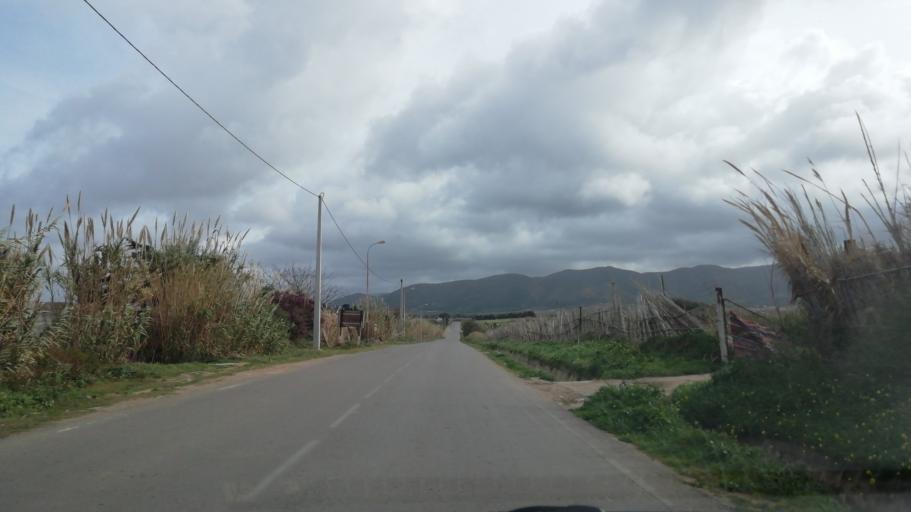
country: DZ
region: Oran
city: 'Ain el Turk
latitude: 35.7009
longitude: -0.8896
